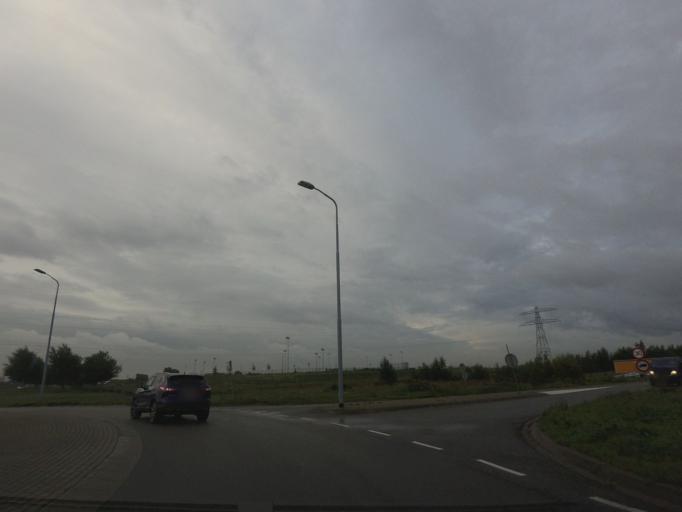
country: NL
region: North Holland
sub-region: Gemeente Bloemendaal
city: Bennebroek
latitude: 52.3024
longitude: 4.6273
